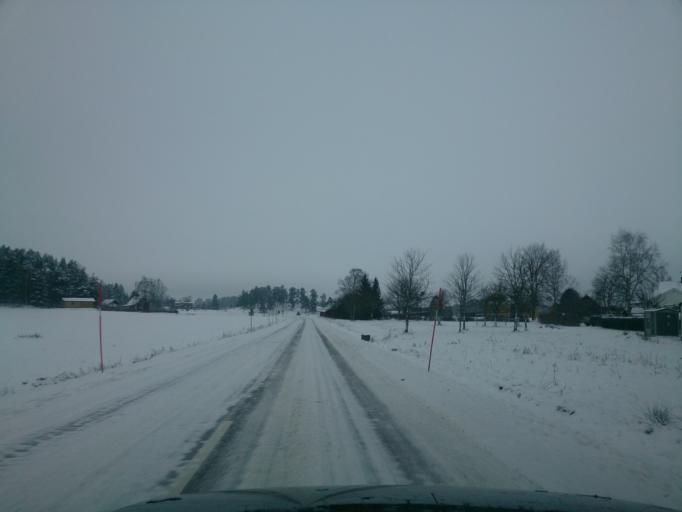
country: SE
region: OEstergoetland
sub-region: Norrkopings Kommun
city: Kimstad
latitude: 58.4119
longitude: 15.9213
